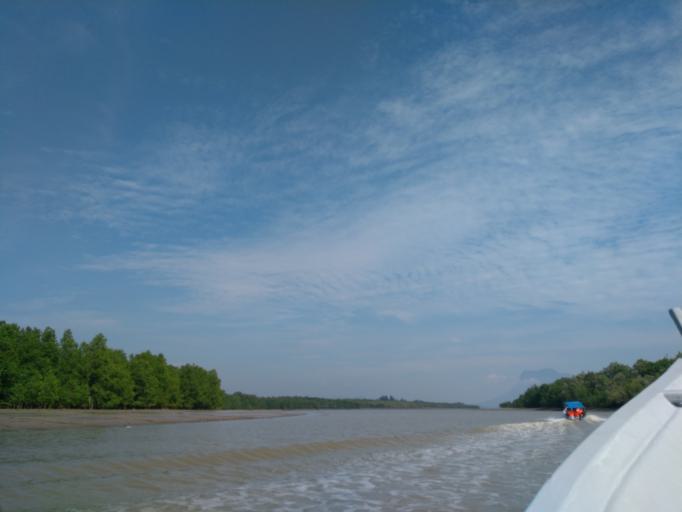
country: MY
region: Sarawak
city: Kuching
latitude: 1.6764
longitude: 110.4321
